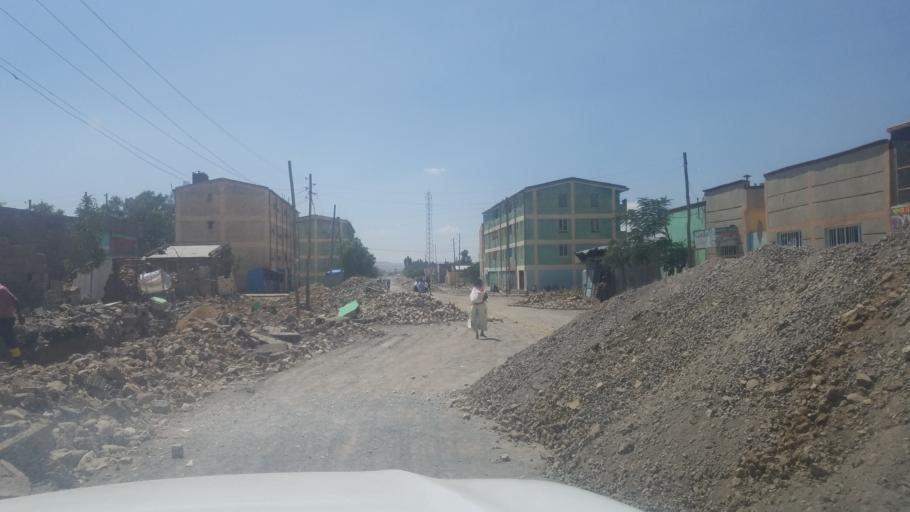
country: ET
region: Tigray
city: Mekele
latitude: 13.7917
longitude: 39.5988
